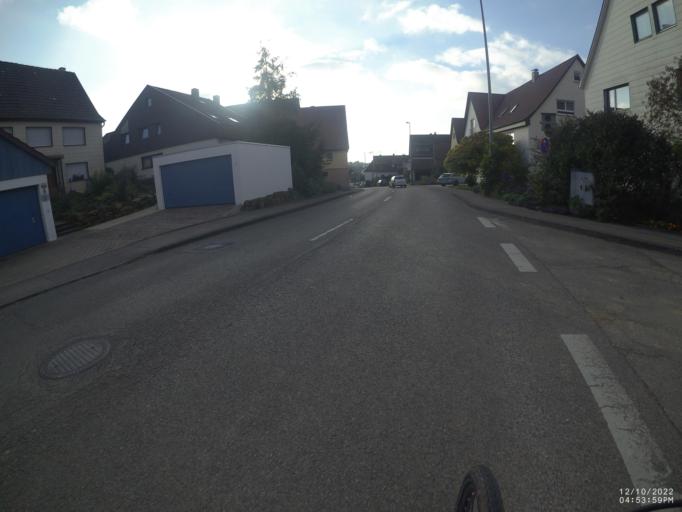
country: DE
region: Baden-Wuerttemberg
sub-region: Regierungsbezirk Stuttgart
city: Albershausen
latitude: 48.7097
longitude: 9.5517
